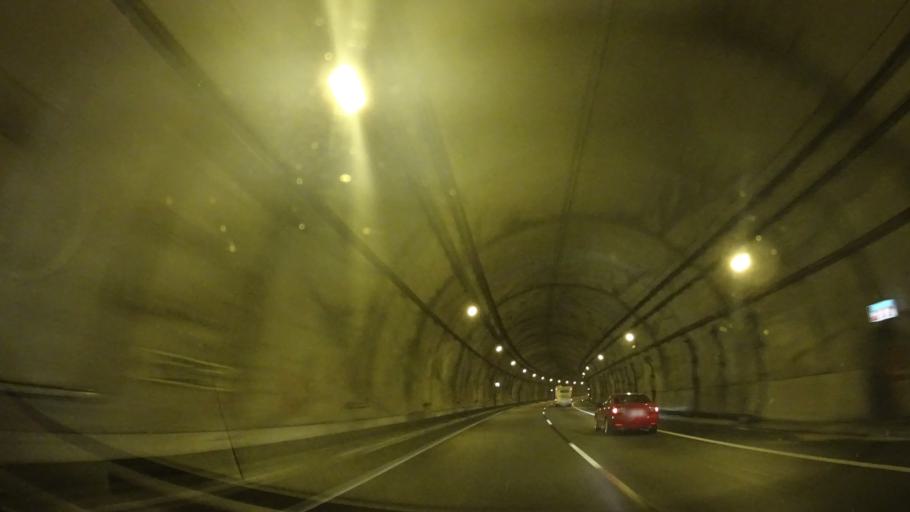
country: ES
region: Asturias
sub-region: Province of Asturias
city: Arriba
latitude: 43.4645
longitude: -5.5174
